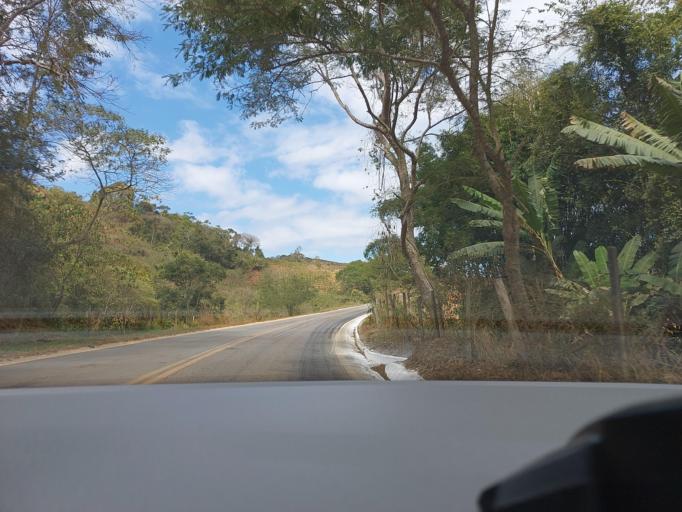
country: BR
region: Minas Gerais
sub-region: Visconde Do Rio Branco
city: Visconde do Rio Branco
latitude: -20.8983
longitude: -42.6535
